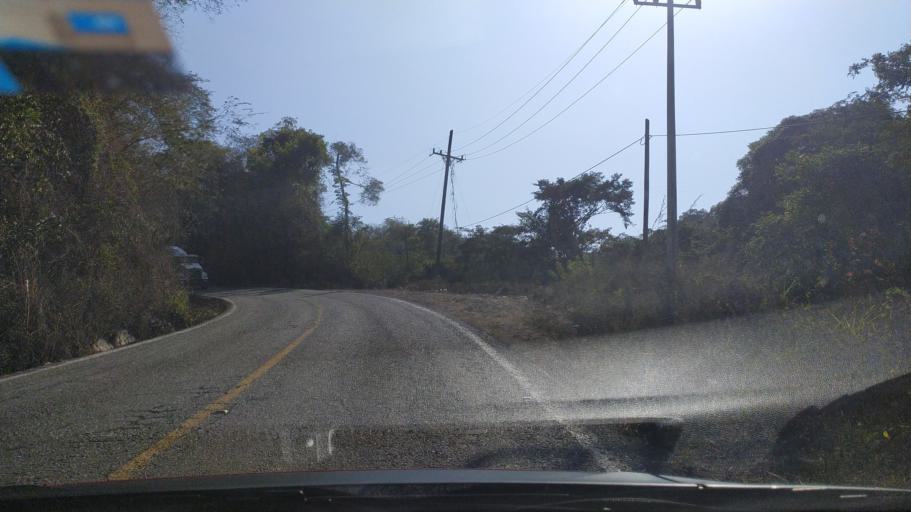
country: MX
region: Michoacan
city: Coahuayana Viejo
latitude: 18.6105
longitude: -103.6780
